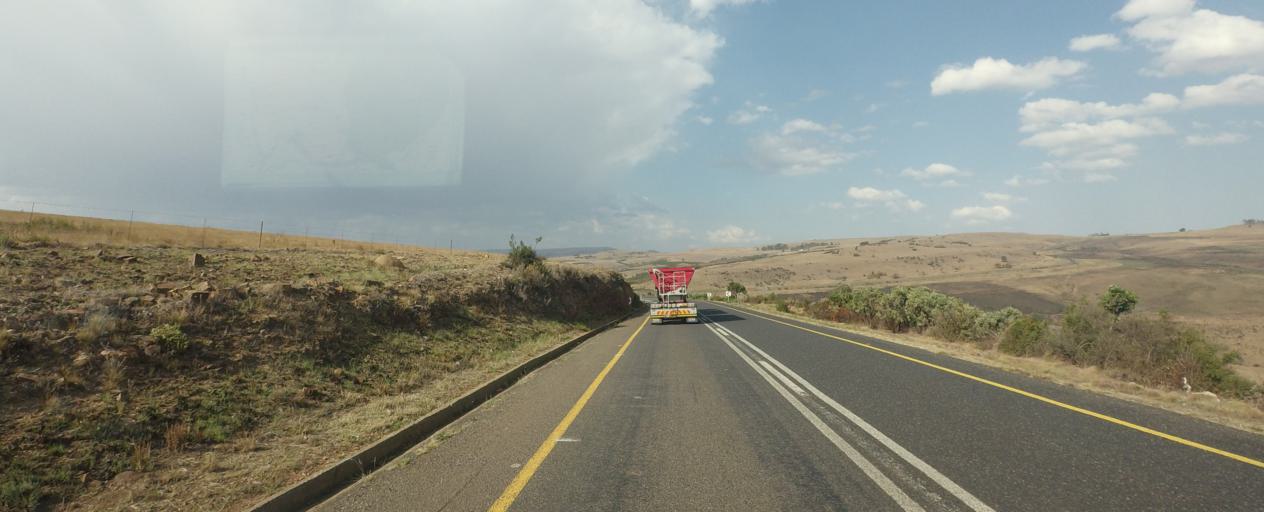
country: ZA
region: Mpumalanga
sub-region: Ehlanzeni District
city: Lydenburg
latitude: -25.1044
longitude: 30.5447
